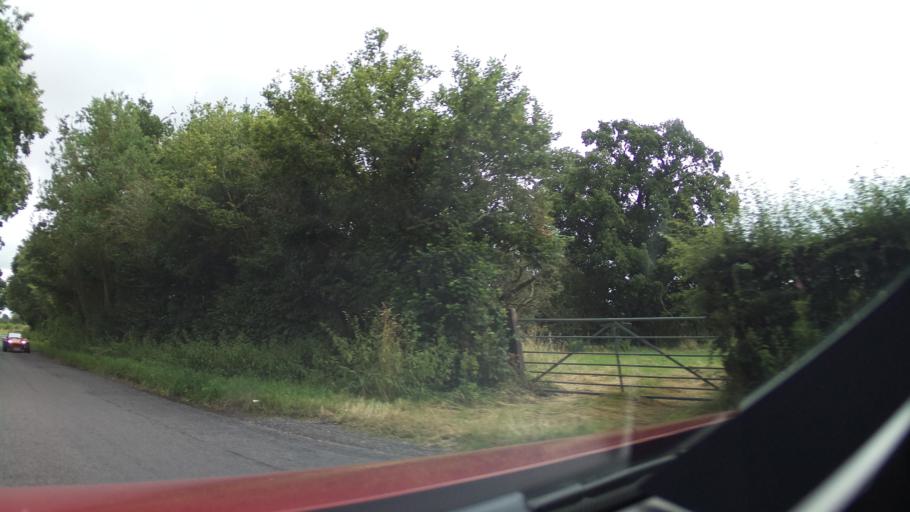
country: GB
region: England
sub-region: Solihull
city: Dickens Heath
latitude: 52.3753
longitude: -1.8312
